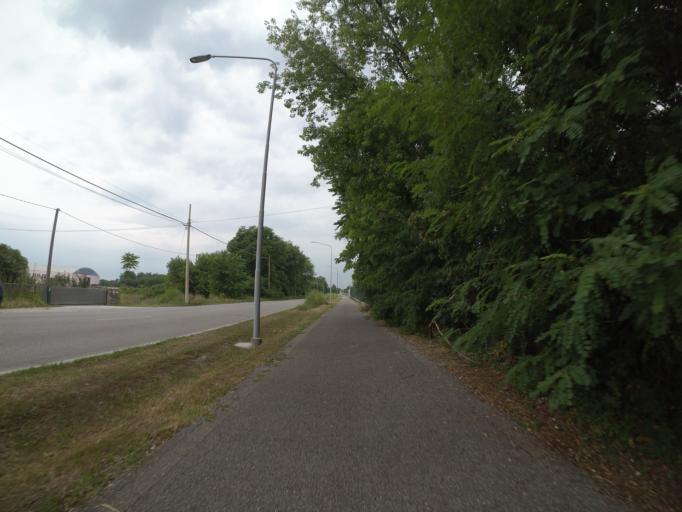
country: IT
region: Friuli Venezia Giulia
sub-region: Provincia di Udine
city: Pasian di Prato
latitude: 46.0512
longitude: 13.1757
